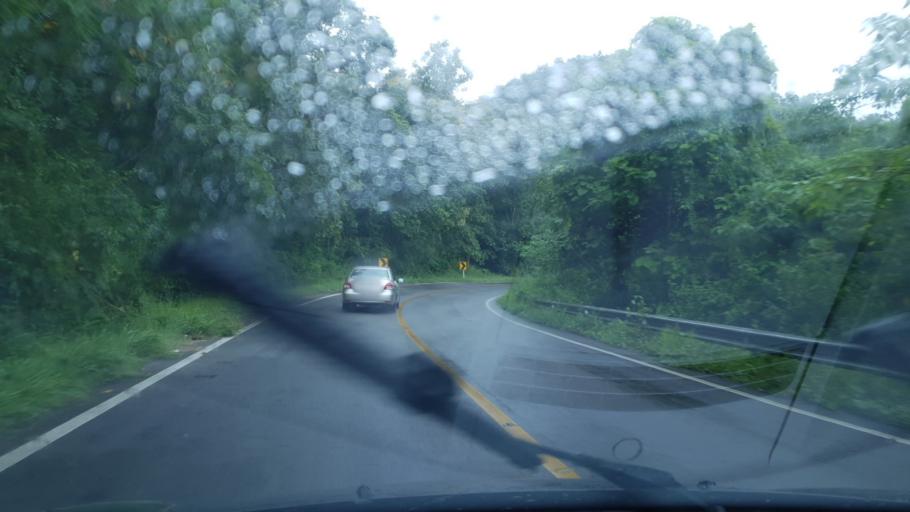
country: TH
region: Mae Hong Son
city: Khun Yuam
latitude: 18.6756
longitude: 97.9243
